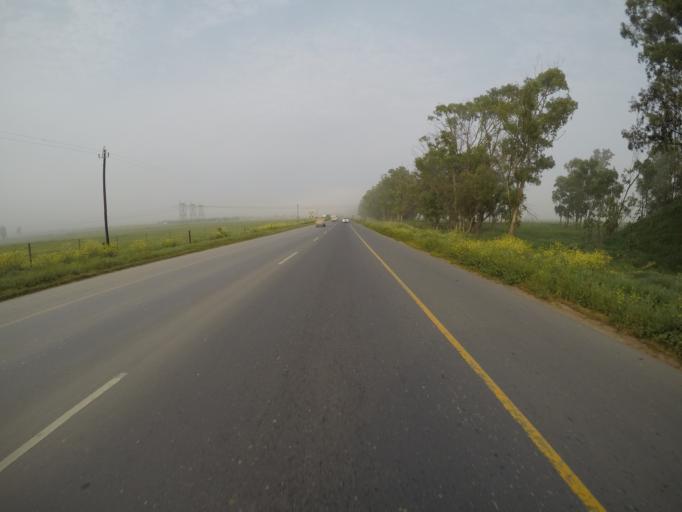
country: ZA
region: Western Cape
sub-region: City of Cape Town
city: Kraaifontein
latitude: -33.7968
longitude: 18.6914
